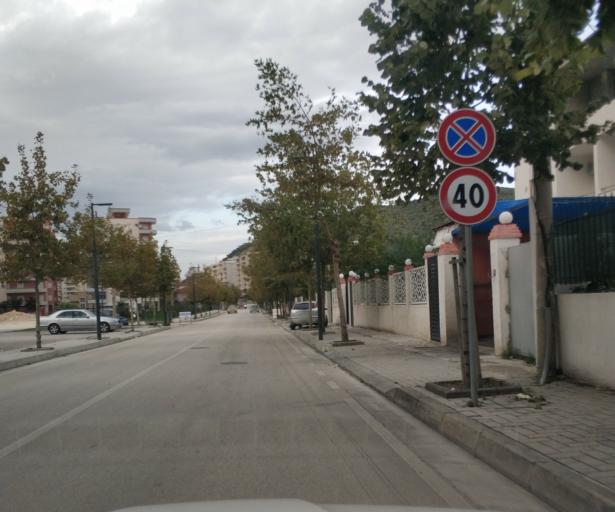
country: AL
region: Vlore
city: Vlore
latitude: 40.4380
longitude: 19.4964
